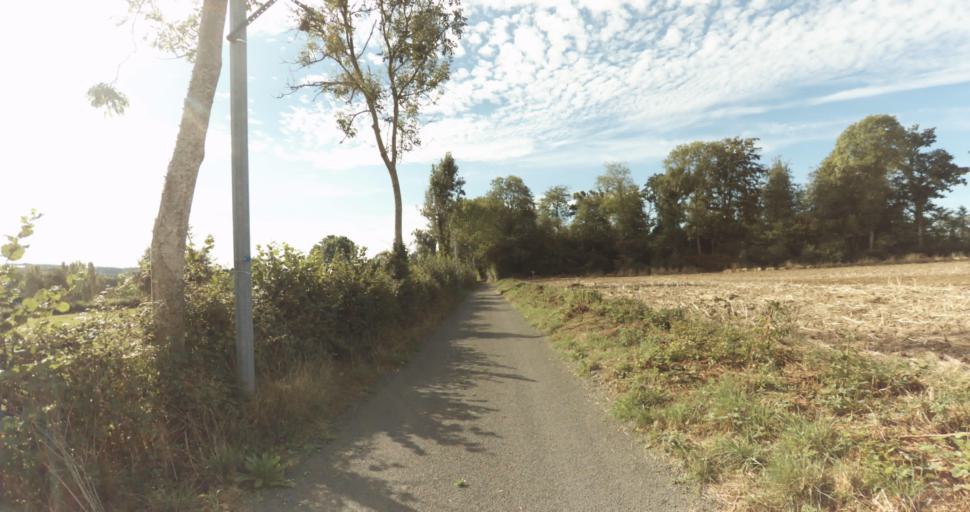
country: FR
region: Lower Normandy
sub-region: Departement de l'Orne
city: Gace
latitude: 48.8256
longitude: 0.2119
